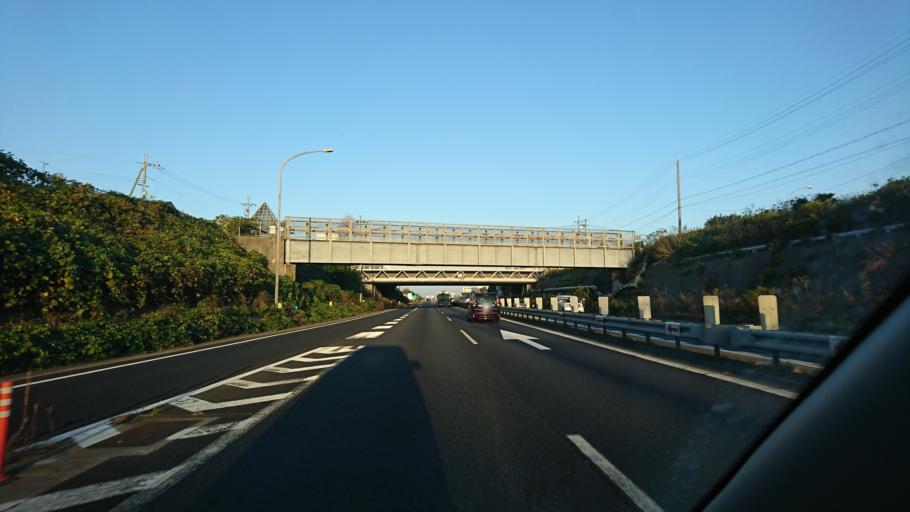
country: JP
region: Hyogo
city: Akashi
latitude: 34.7106
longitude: 134.9429
